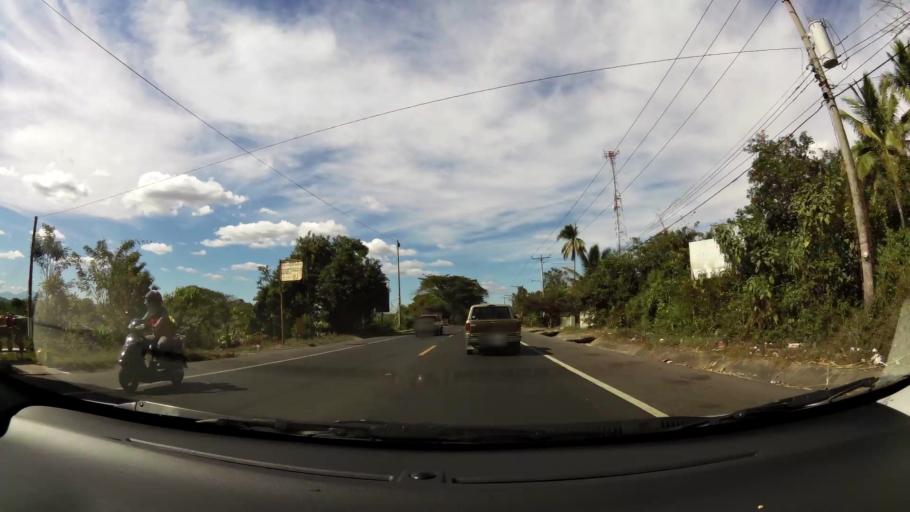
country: SV
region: San Salvador
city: Guazapa
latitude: 13.8703
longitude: -89.1708
